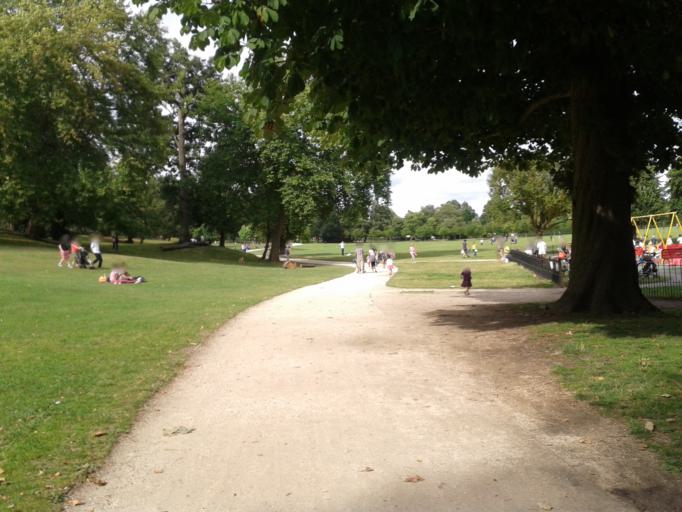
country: GB
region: England
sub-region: Greater London
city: Thornton Heath
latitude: 51.4200
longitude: -0.0656
